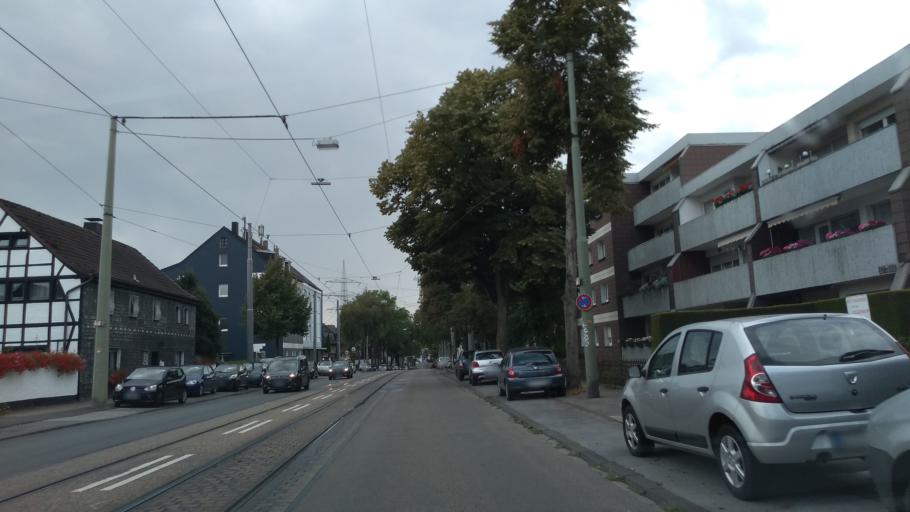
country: DE
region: North Rhine-Westphalia
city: Hattingen
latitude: 51.4377
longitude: 7.1837
